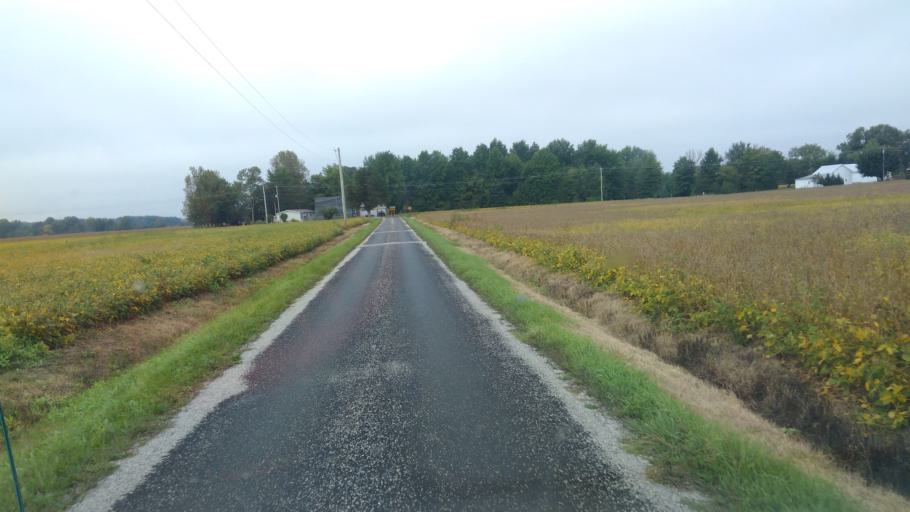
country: US
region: Ohio
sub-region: Morrow County
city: Cardington
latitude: 40.5503
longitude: -82.9934
